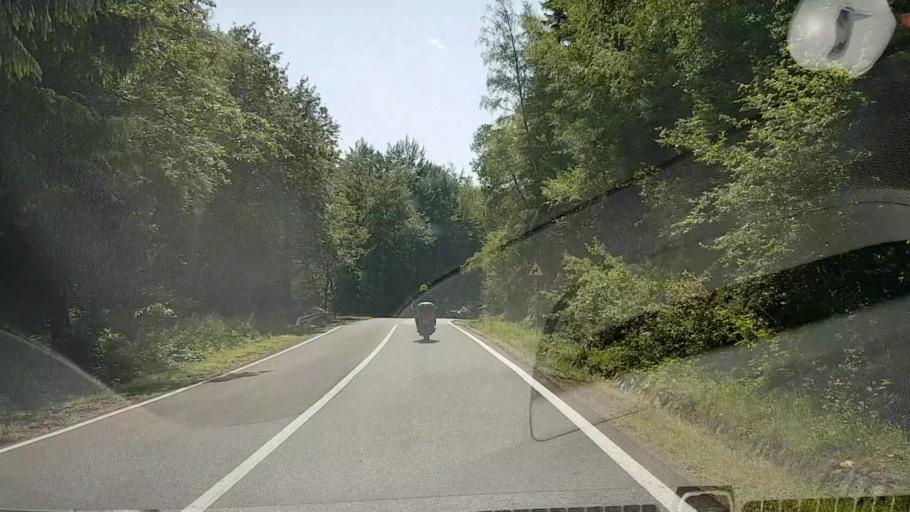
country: RO
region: Sibiu
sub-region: Comuna Cartisoara
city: Cartisoara
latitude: 45.6615
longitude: 24.5949
